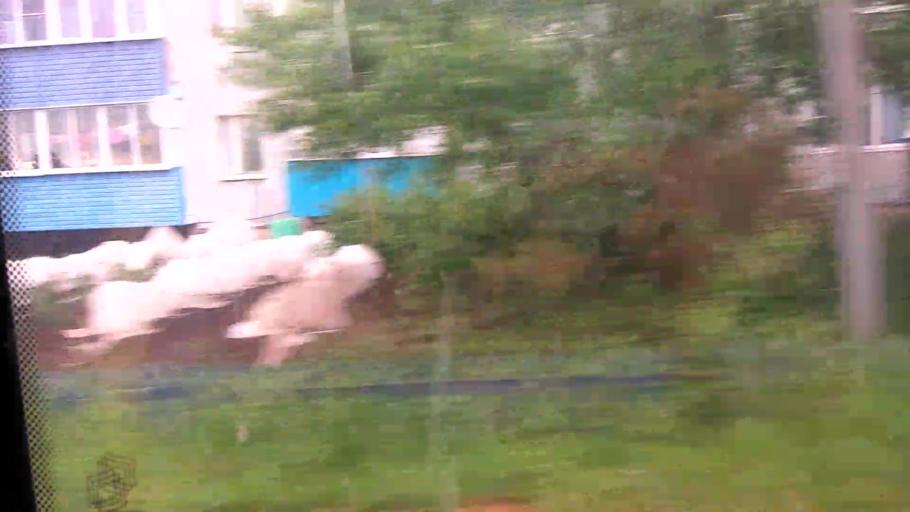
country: RU
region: Moskovskaya
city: Ozery
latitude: 54.7718
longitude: 38.6418
